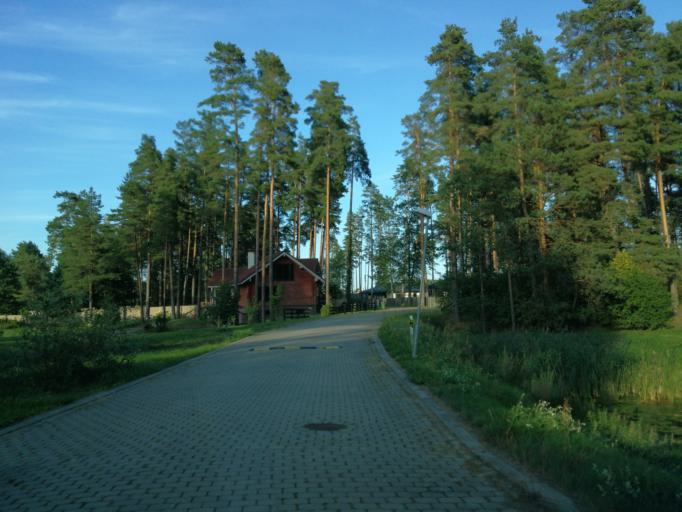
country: LV
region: Garkalne
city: Garkalne
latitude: 57.0852
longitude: 24.4729
